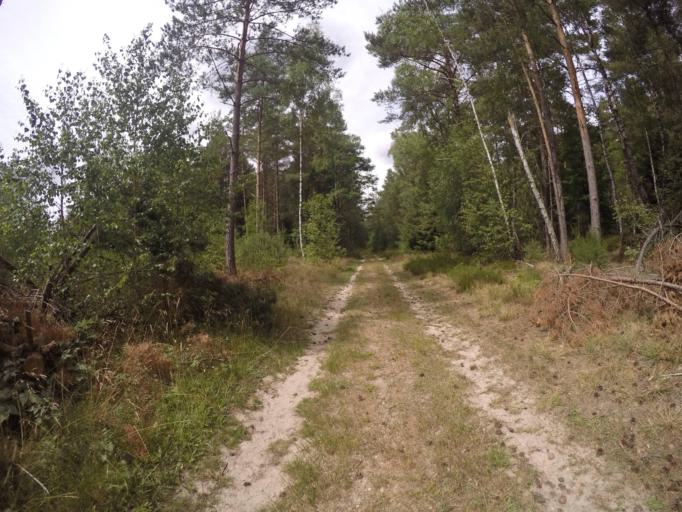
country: DE
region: Lower Saxony
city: Thomasburg
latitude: 53.2523
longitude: 10.6845
